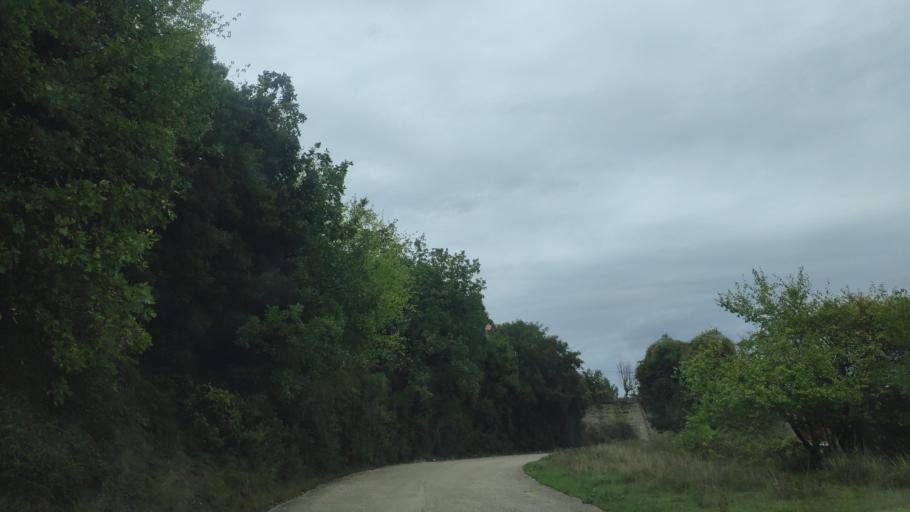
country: GR
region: Epirus
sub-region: Nomos Thesprotias
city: Paramythia
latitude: 39.4611
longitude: 20.6756
